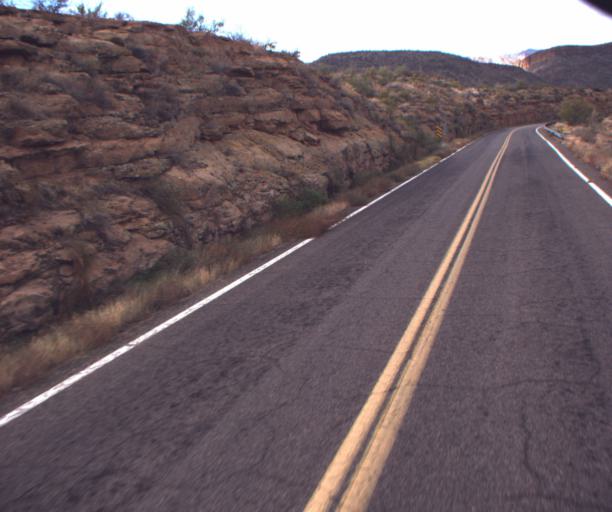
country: US
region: Arizona
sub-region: Pinal County
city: Apache Junction
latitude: 33.5330
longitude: -111.3576
